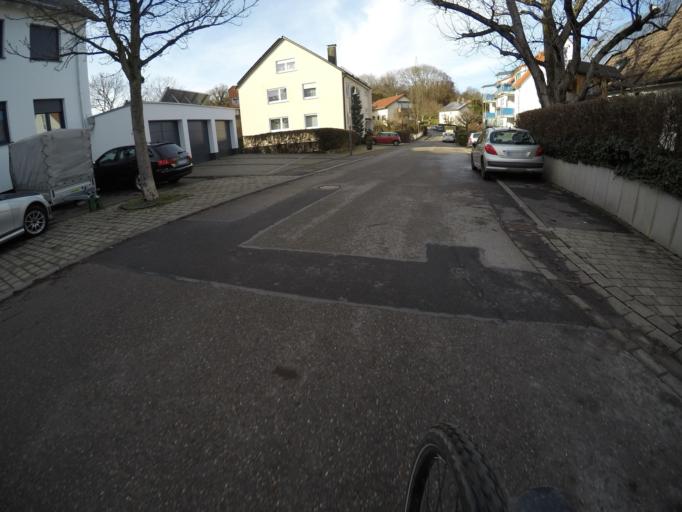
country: DE
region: Baden-Wuerttemberg
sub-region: Regierungsbezirk Stuttgart
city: Dettingen unter Teck
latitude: 48.6194
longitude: 9.4498
